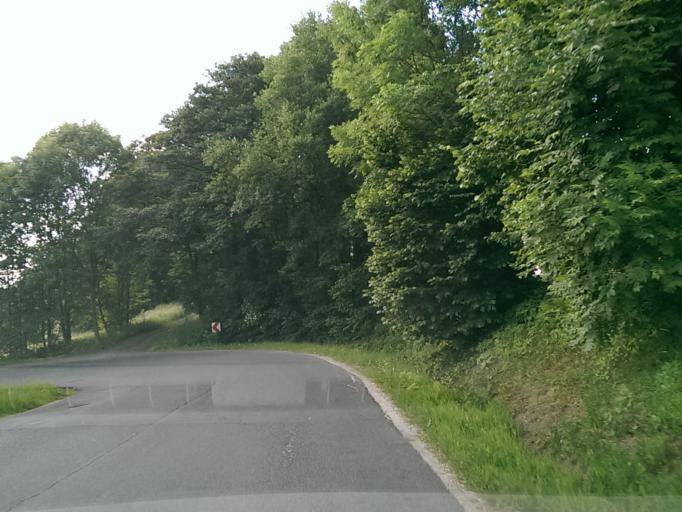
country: CZ
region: Liberecky
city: Semily
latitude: 50.5827
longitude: 15.2952
